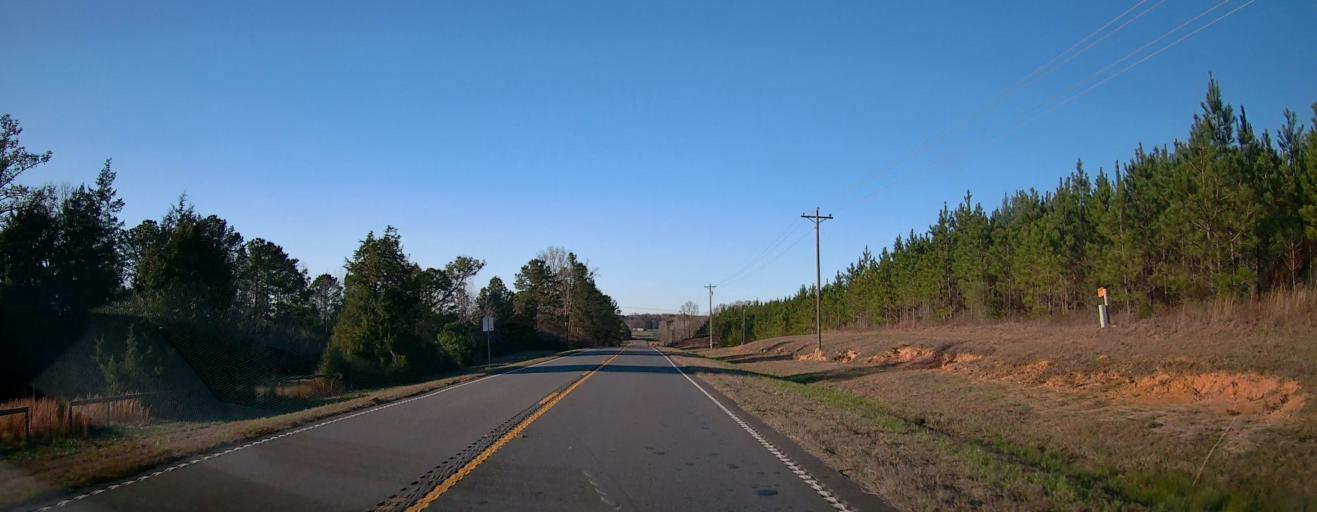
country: US
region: Georgia
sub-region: Talbot County
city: Talbotton
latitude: 32.5880
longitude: -84.5541
